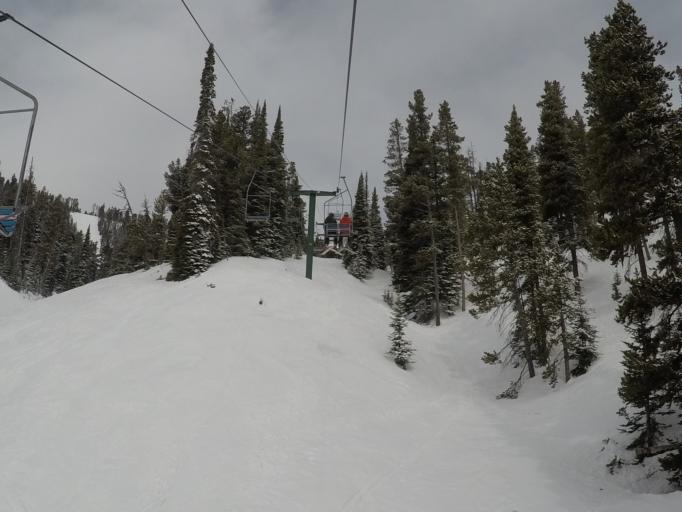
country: US
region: Montana
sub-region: Meagher County
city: White Sulphur Springs
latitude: 46.8332
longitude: -110.7089
